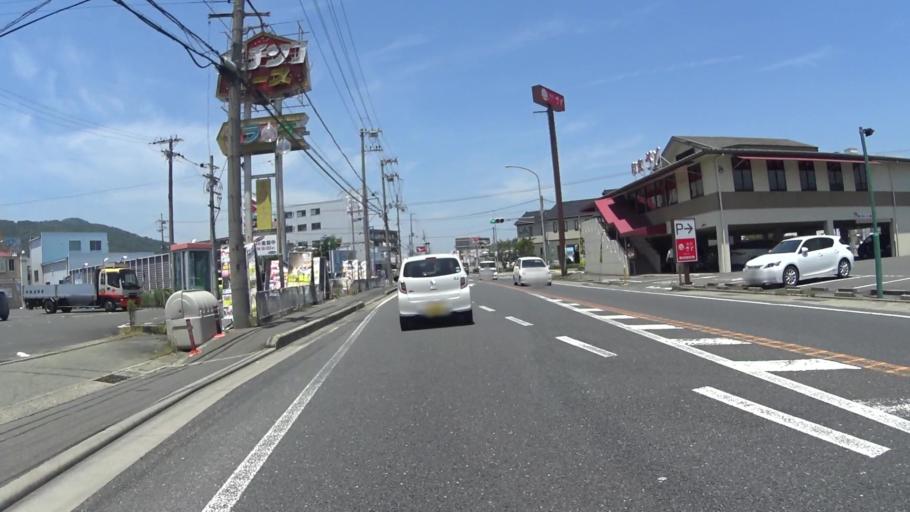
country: JP
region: Kyoto
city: Kameoka
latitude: 35.0299
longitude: 135.5539
